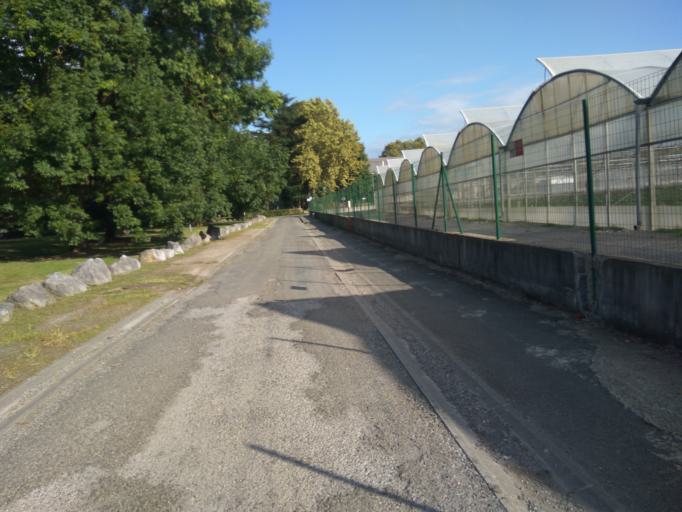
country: FR
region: Aquitaine
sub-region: Departement des Pyrenees-Atlantiques
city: Gelos
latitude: 43.2871
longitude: -0.3712
